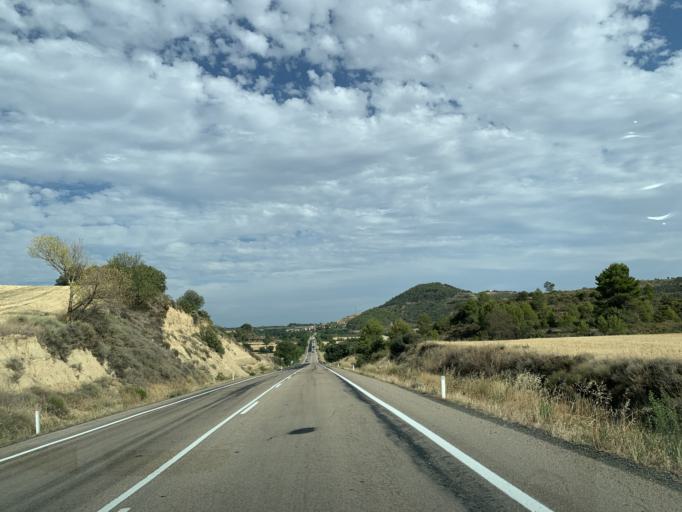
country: ES
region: Aragon
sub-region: Provincia de Huesca
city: Ayerbe
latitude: 42.2862
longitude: -0.7103
